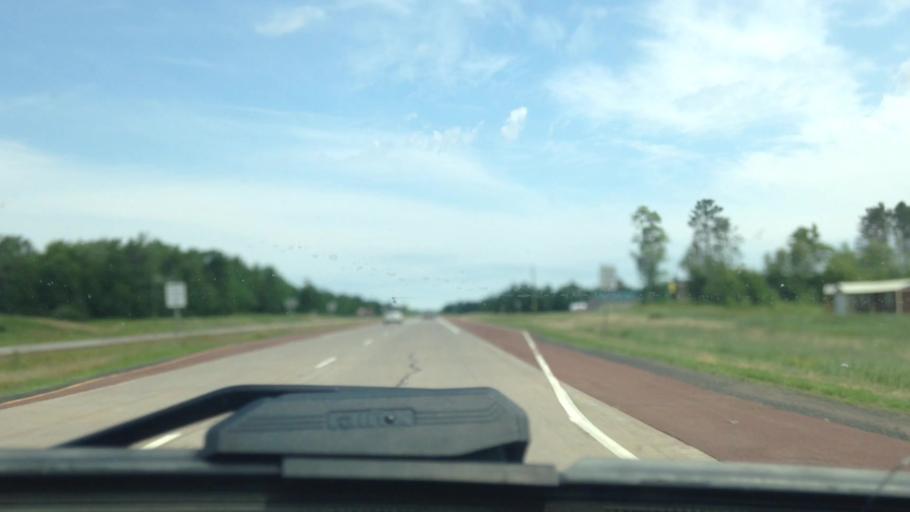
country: US
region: Wisconsin
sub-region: Douglas County
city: Lake Nebagamon
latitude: 46.3584
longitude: -91.8329
